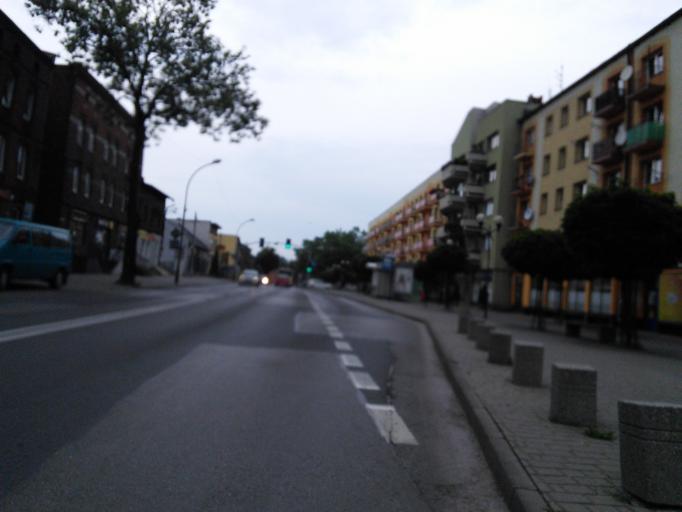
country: PL
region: Silesian Voivodeship
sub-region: Piekary Slaskie
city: Brzeziny Slaskie
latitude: 50.3668
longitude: 18.9819
